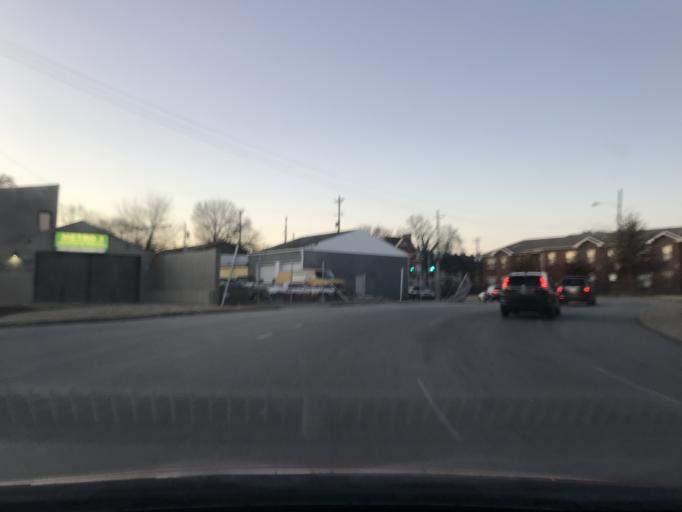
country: US
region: Kentucky
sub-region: Jefferson County
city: Louisville
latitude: 38.2355
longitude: -85.7484
